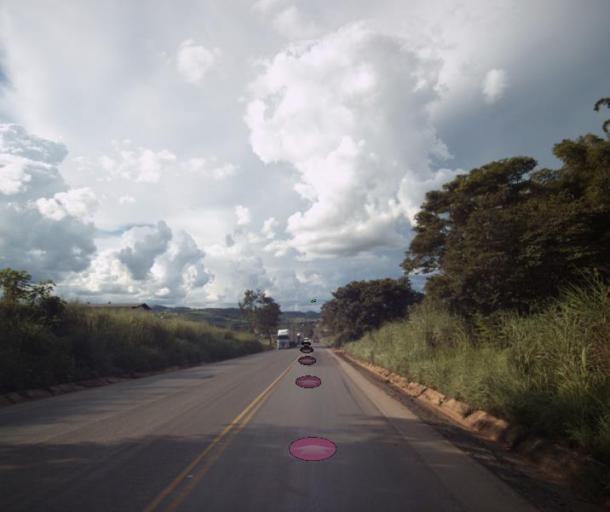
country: BR
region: Goias
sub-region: Rialma
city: Rialma
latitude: -15.3131
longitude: -49.5726
